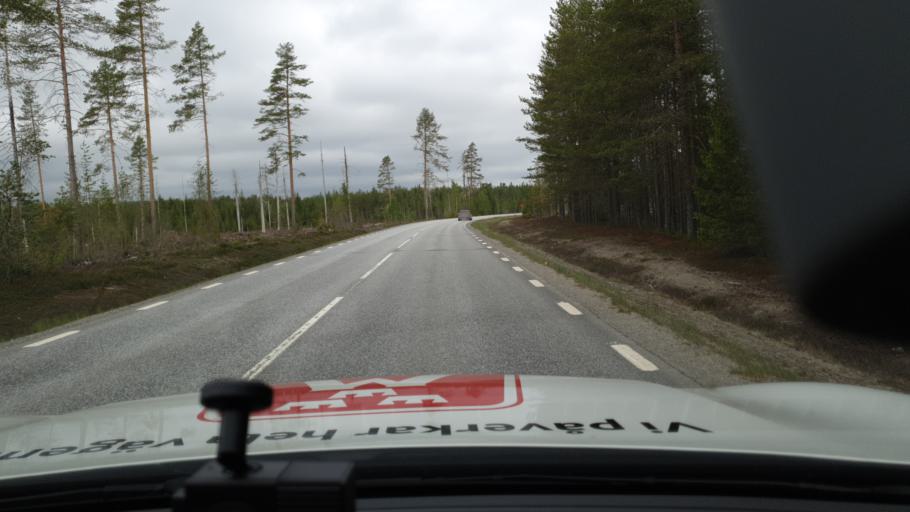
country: SE
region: Vaesterbotten
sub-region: Umea Kommun
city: Roback
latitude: 63.9460
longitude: 20.1451
